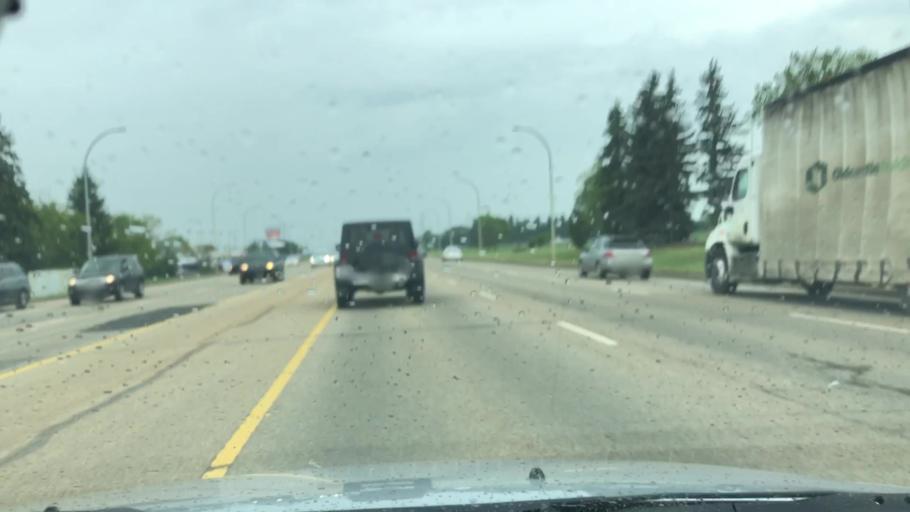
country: CA
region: Alberta
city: St. Albert
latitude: 53.6085
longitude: -113.5856
